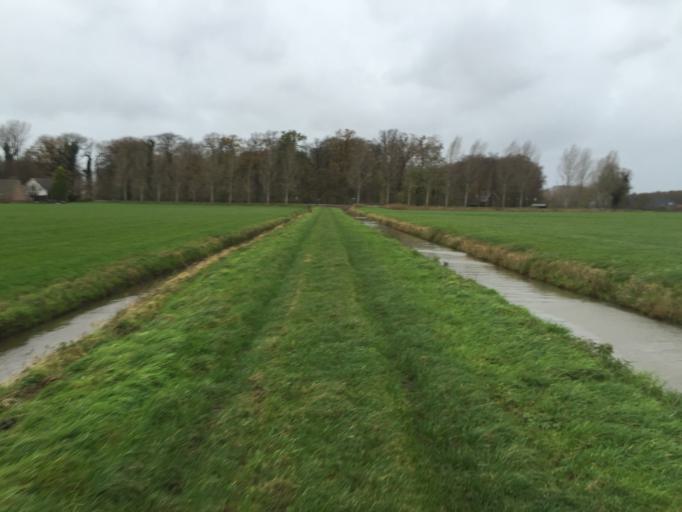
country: NL
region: Utrecht
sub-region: Gemeente Woerden
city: Woerden
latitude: 52.0519
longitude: 4.9081
